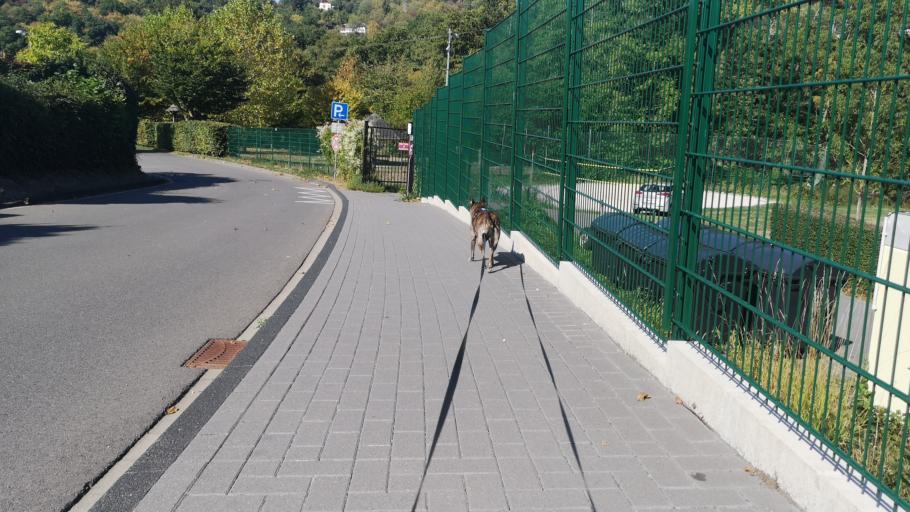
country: DE
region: North Rhine-Westphalia
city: Heimbach
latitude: 50.6380
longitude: 6.4700
